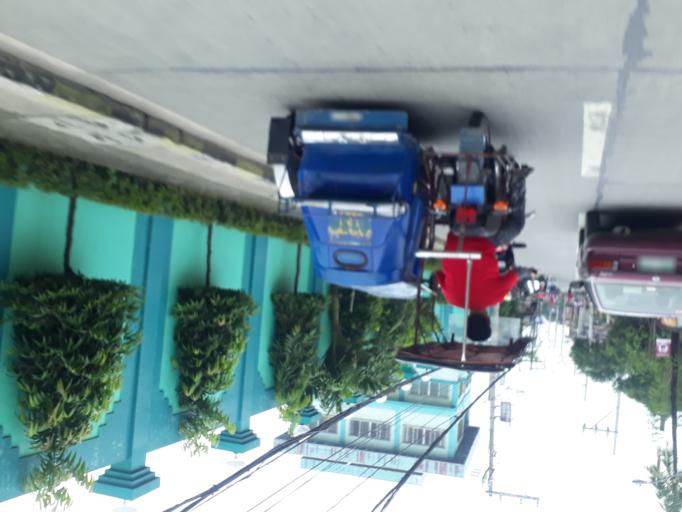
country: PH
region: Calabarzon
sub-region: Province of Rizal
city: Valenzuela
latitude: 14.7037
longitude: 120.9552
